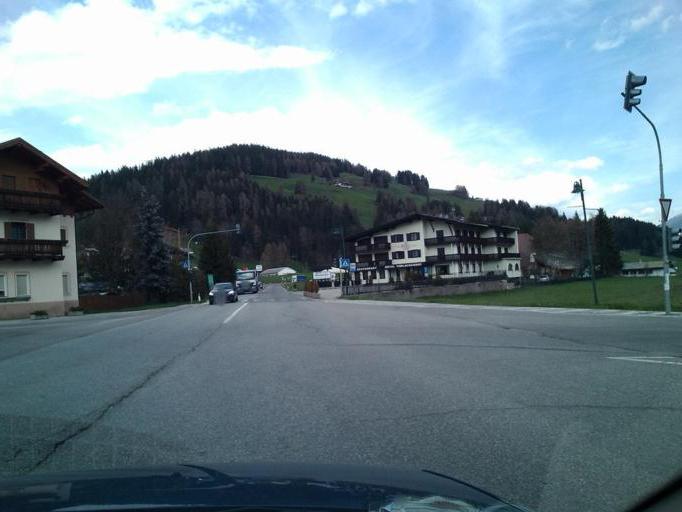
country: IT
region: Trentino-Alto Adige
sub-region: Bolzano
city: Dobbiaco
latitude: 46.7290
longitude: 12.2233
